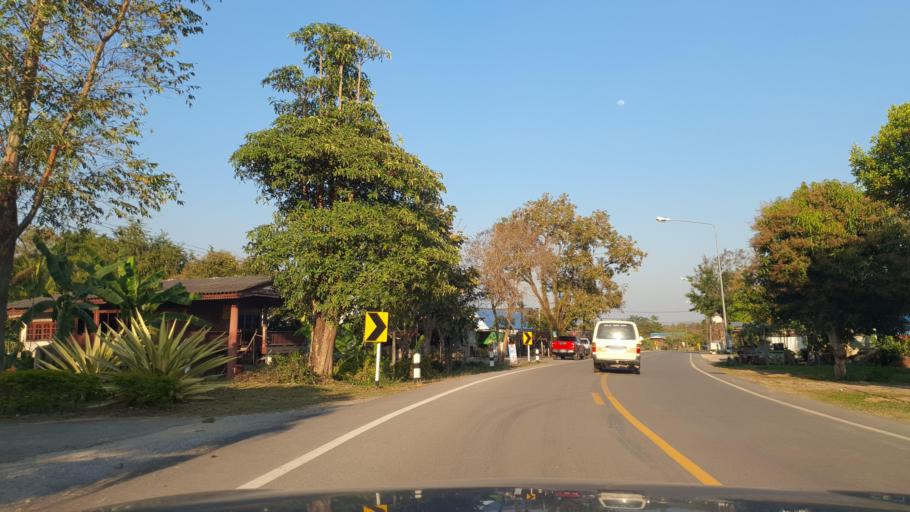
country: TH
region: Chiang Rai
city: Mae Lao
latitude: 19.8343
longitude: 99.6942
